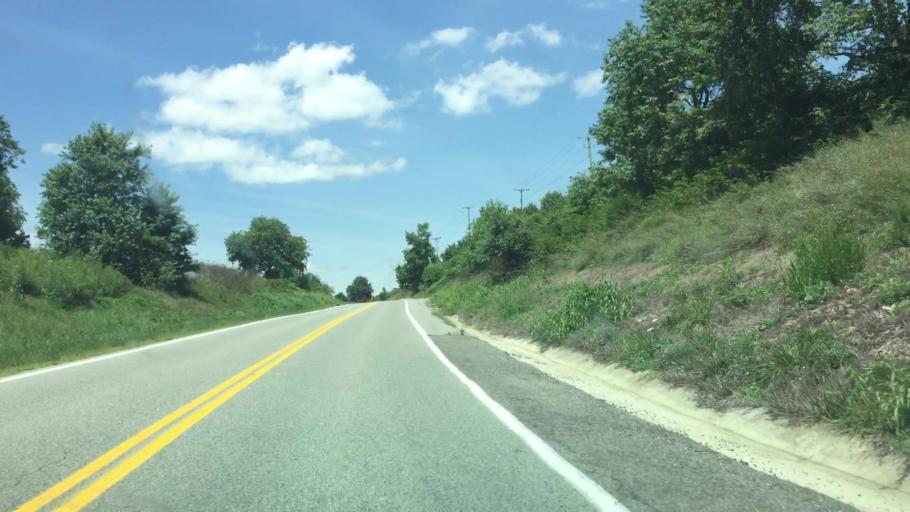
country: US
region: Virginia
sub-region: Wythe County
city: Wytheville
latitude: 36.9495
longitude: -80.9209
